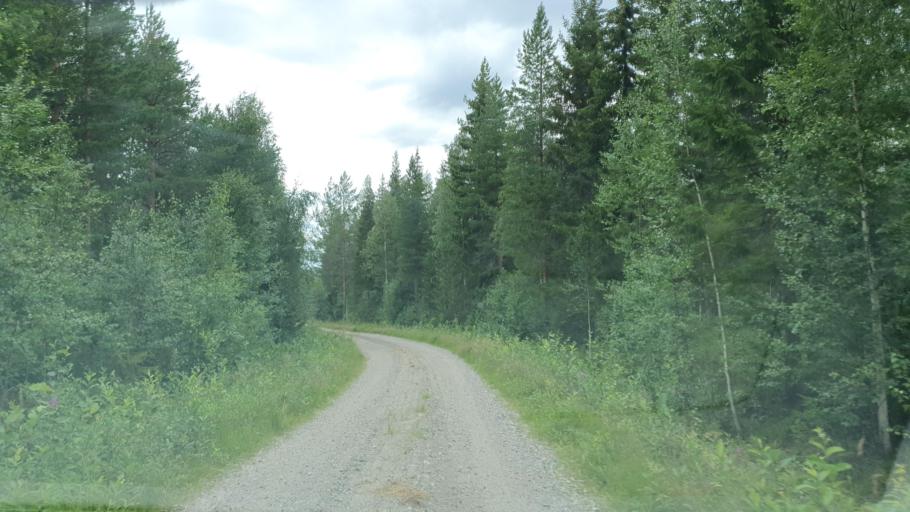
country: FI
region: Kainuu
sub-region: Kehys-Kainuu
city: Kuhmo
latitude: 64.2032
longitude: 29.4010
